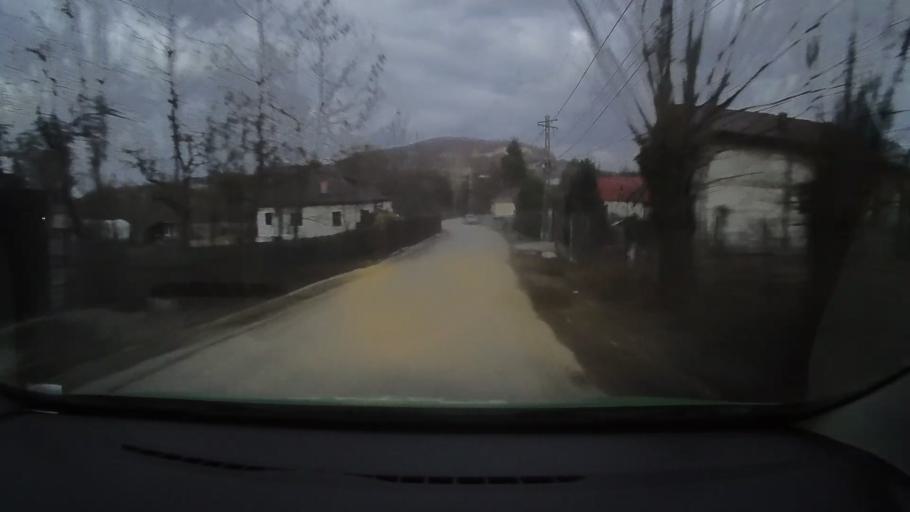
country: RO
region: Prahova
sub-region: Comuna Provita de Sus
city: Provita de Sus
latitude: 45.1394
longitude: 25.6263
